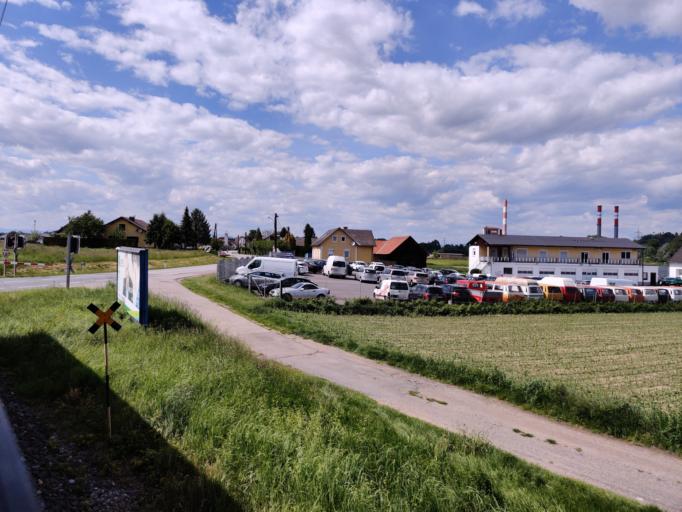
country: AT
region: Styria
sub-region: Politischer Bezirk Leibnitz
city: Weitendorf
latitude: 46.8958
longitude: 15.4908
